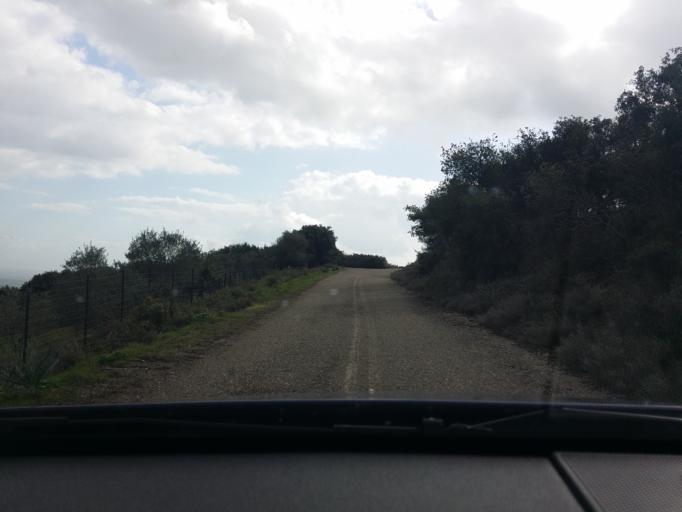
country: GR
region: West Greece
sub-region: Nomos Aitolias kai Akarnanias
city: Fitiai
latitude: 38.6743
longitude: 21.1911
